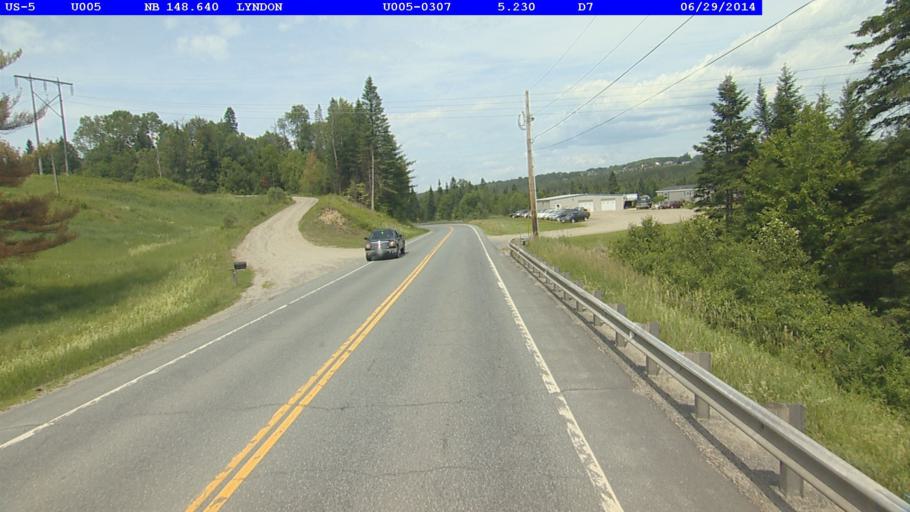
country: US
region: Vermont
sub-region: Caledonia County
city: Lyndonville
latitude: 44.5630
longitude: -71.9905
